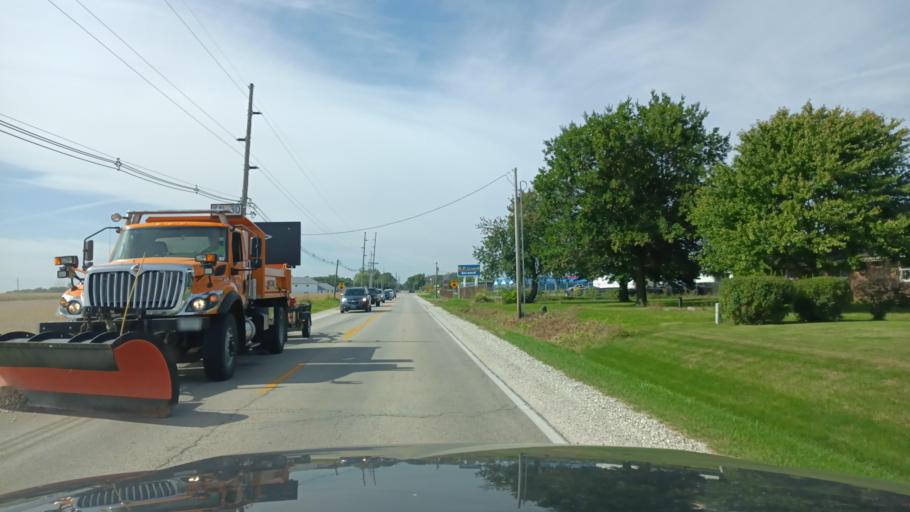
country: US
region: Illinois
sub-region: Knox County
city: Knoxville
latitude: 40.9158
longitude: -90.3042
